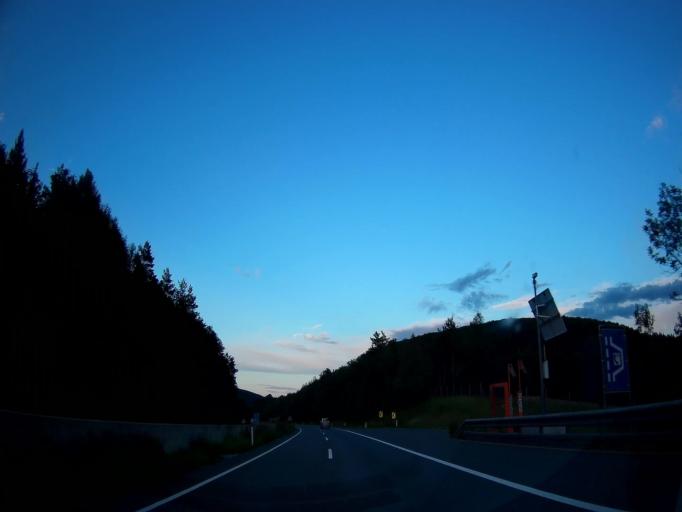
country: AT
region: Lower Austria
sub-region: Politischer Bezirk Wien-Umgebung
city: Pressbaum
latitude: 48.1751
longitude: 16.1021
